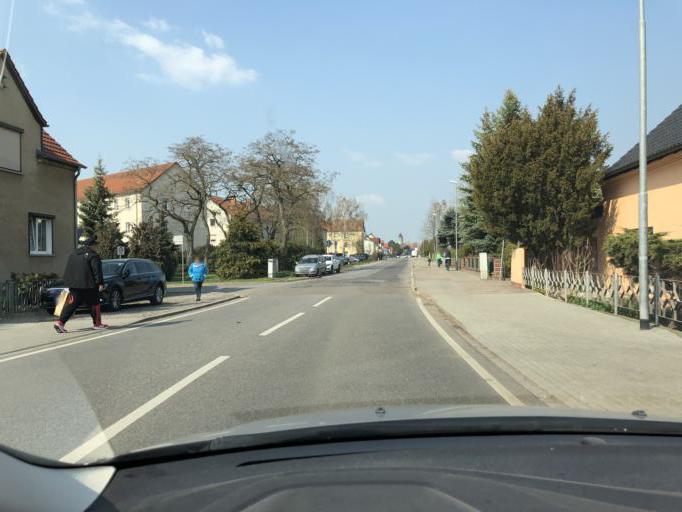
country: DE
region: Saxony-Anhalt
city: Hohenthurm
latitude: 51.5131
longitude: 12.0970
